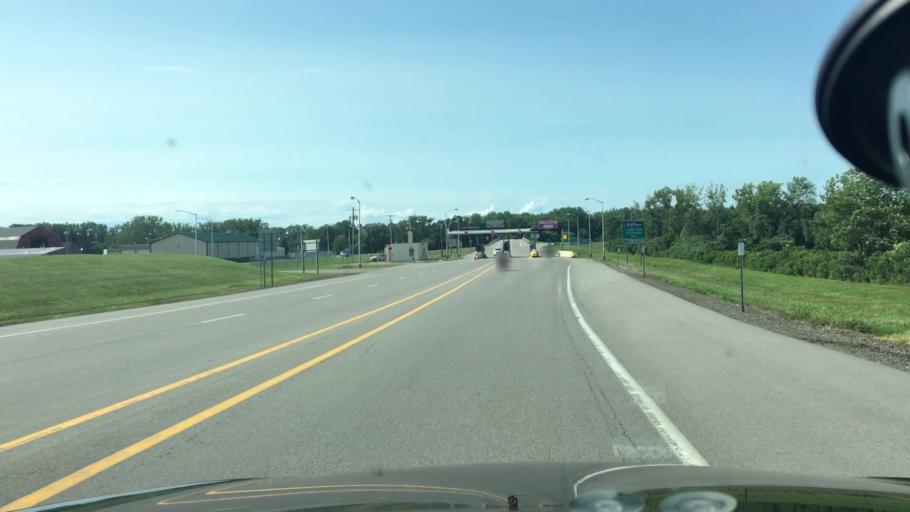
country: US
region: New York
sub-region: Chautauqua County
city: Silver Creek
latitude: 42.5586
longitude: -79.1146
